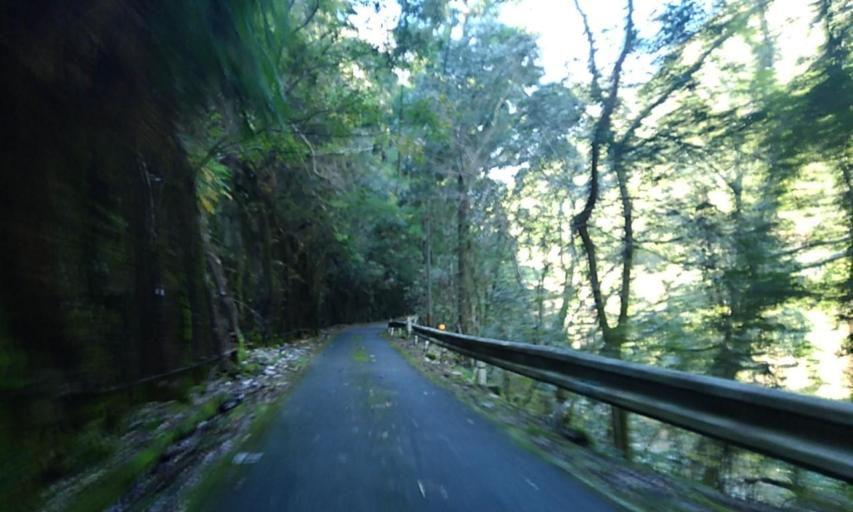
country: JP
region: Wakayama
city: Shingu
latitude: 33.9093
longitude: 135.9945
